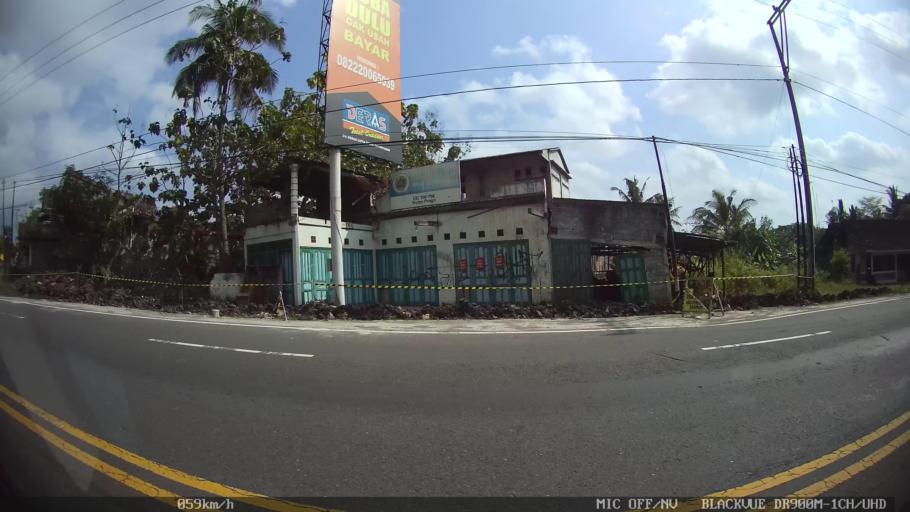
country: ID
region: Daerah Istimewa Yogyakarta
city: Srandakan
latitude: -7.8660
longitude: 110.1697
